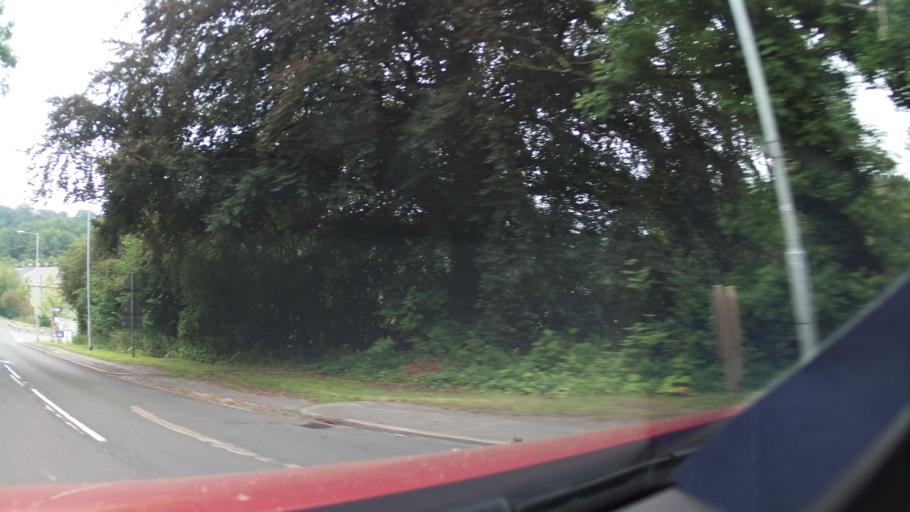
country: GB
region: England
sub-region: Staffordshire
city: Cheadle
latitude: 53.0238
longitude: -1.9623
